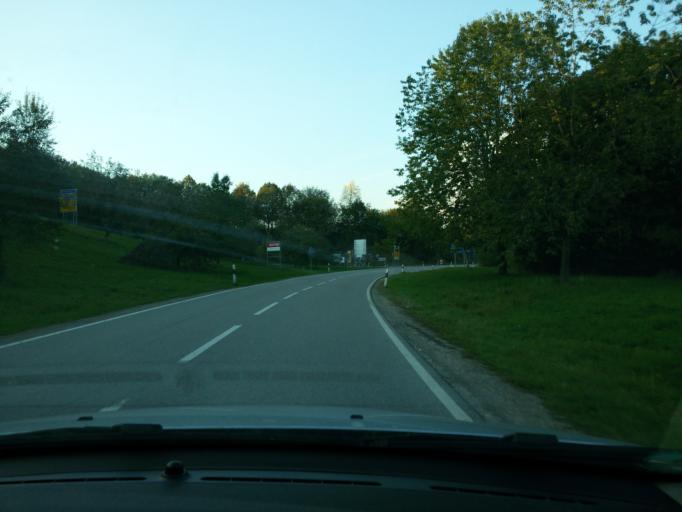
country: DE
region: Bavaria
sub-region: Swabia
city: Stetten
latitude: 48.0302
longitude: 10.4413
